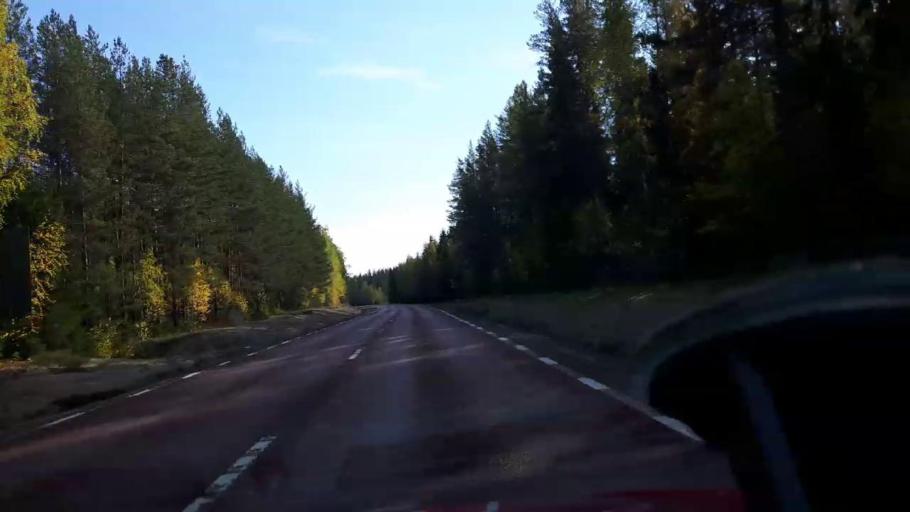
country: SE
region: Gaevleborg
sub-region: Ljusdals Kommun
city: Farila
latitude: 61.9263
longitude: 15.5745
